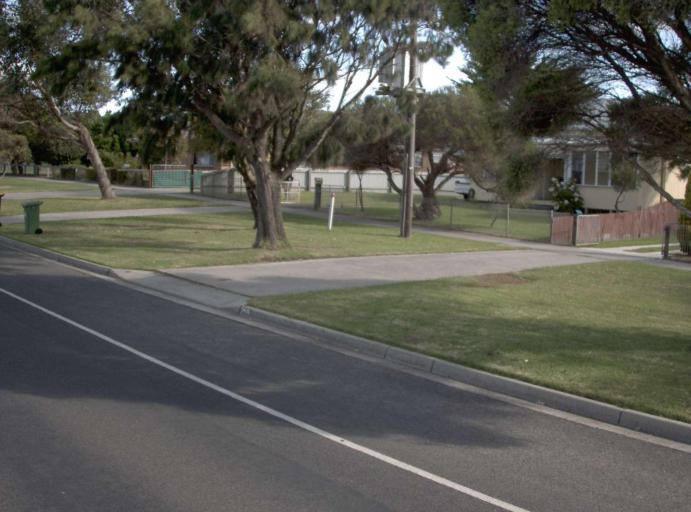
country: AU
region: Victoria
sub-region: Bass Coast
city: North Wonthaggi
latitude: -38.5911
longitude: 145.5857
